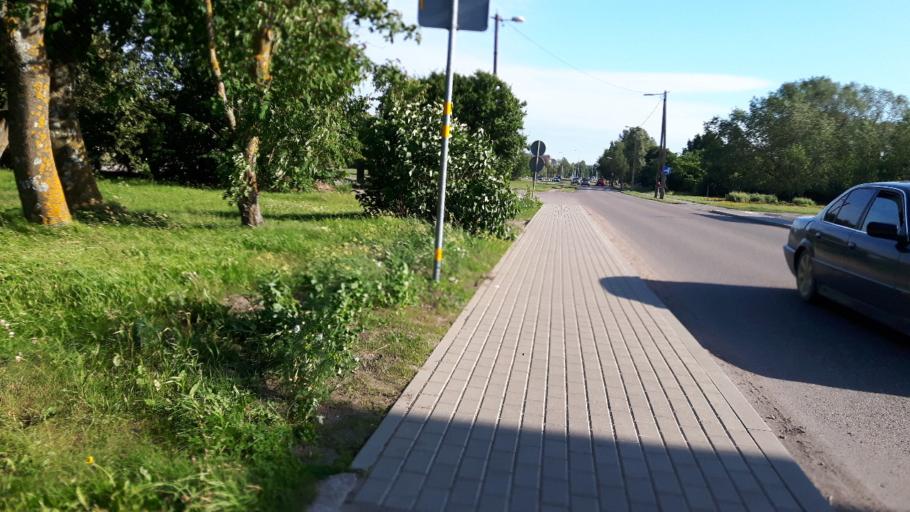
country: LV
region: Liepaja
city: Vec-Liepaja
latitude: 56.5446
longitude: 21.0045
